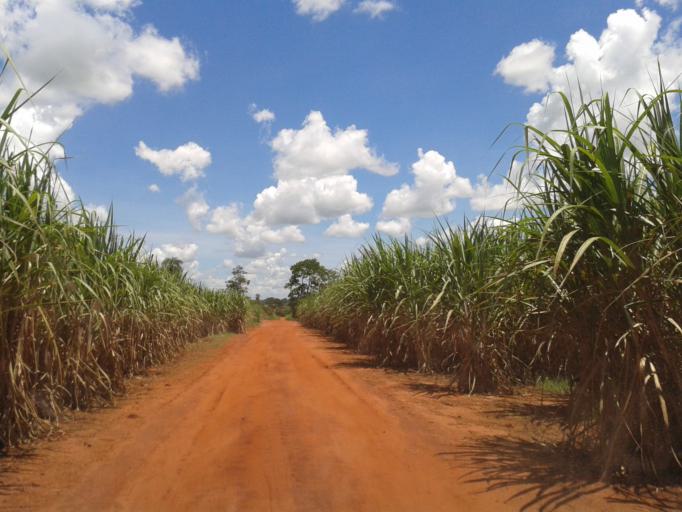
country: BR
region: Minas Gerais
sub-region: Capinopolis
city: Capinopolis
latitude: -18.7945
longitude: -49.8269
